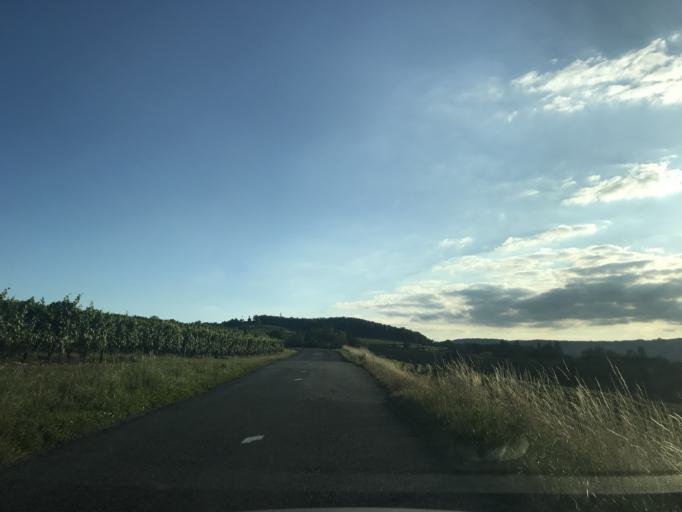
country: FR
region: Rhone-Alpes
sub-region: Departement de la Savoie
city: Yenne
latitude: 45.7354
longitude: 5.7994
